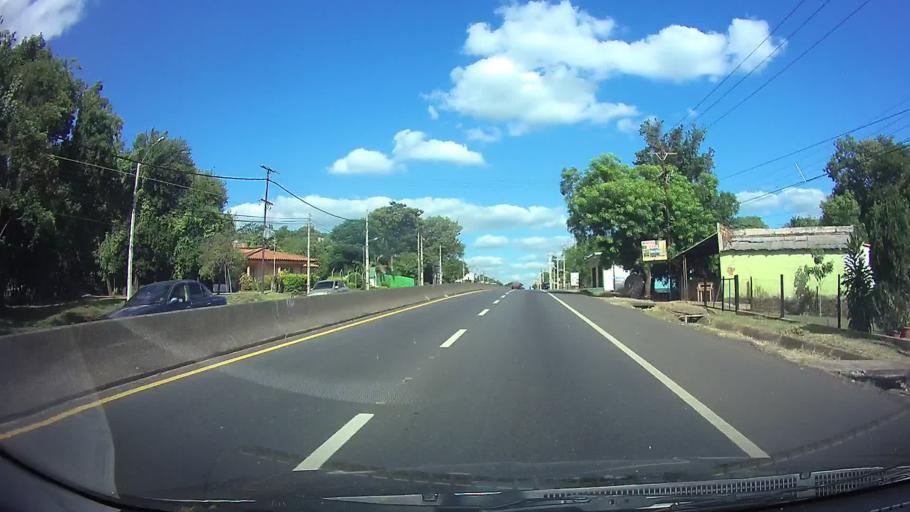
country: PY
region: Central
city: Itaugua
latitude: -25.3985
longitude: -57.3320
